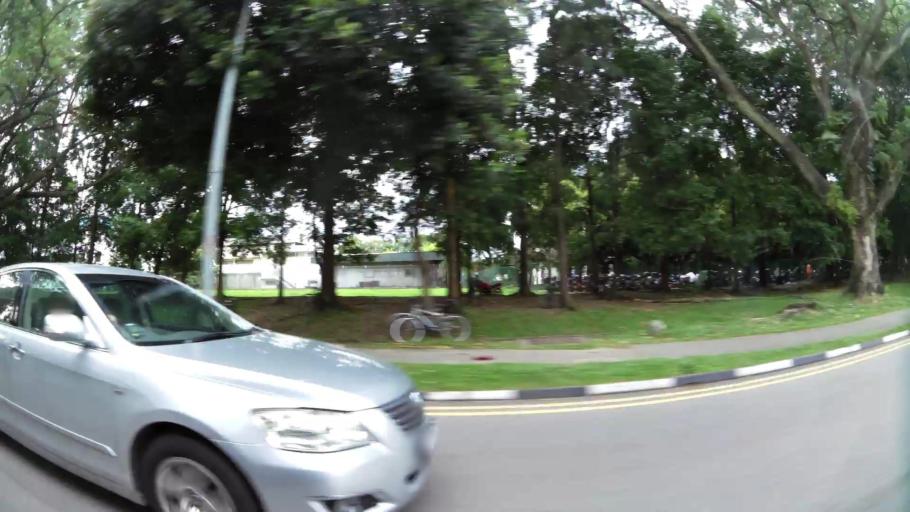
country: MY
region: Johor
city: Kampung Pasir Gudang Baru
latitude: 1.4609
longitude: 103.8197
